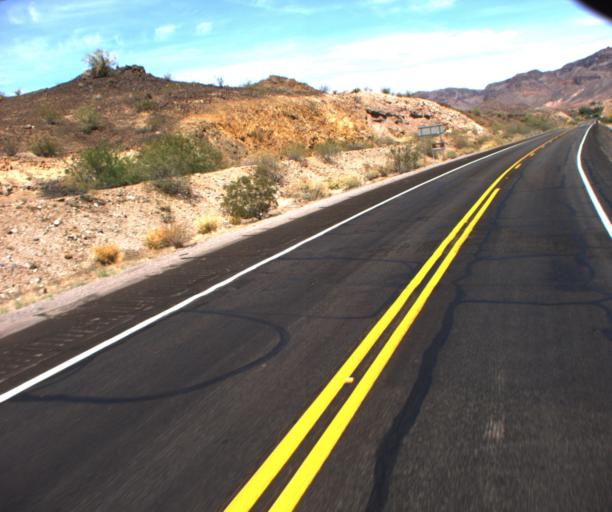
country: US
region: Arizona
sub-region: La Paz County
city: Cienega Springs
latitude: 34.2551
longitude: -114.1595
